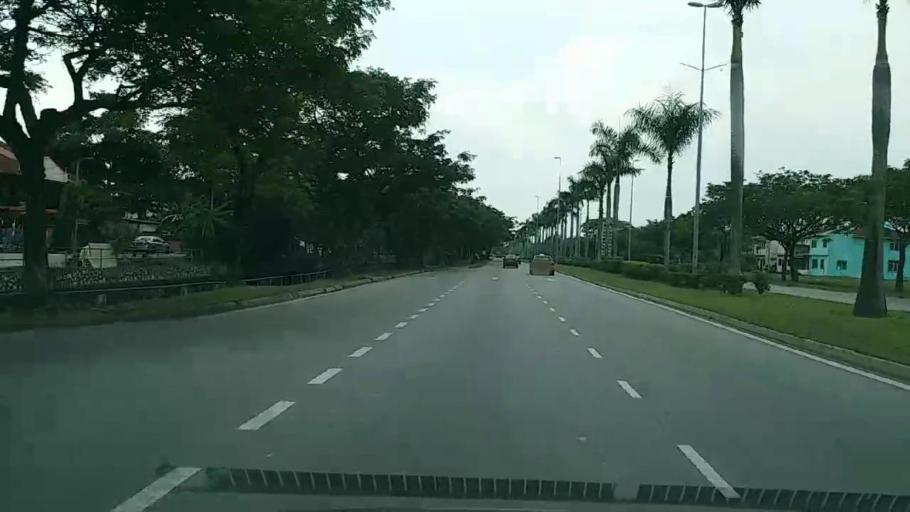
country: MY
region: Putrajaya
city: Putrajaya
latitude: 2.9403
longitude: 101.6179
